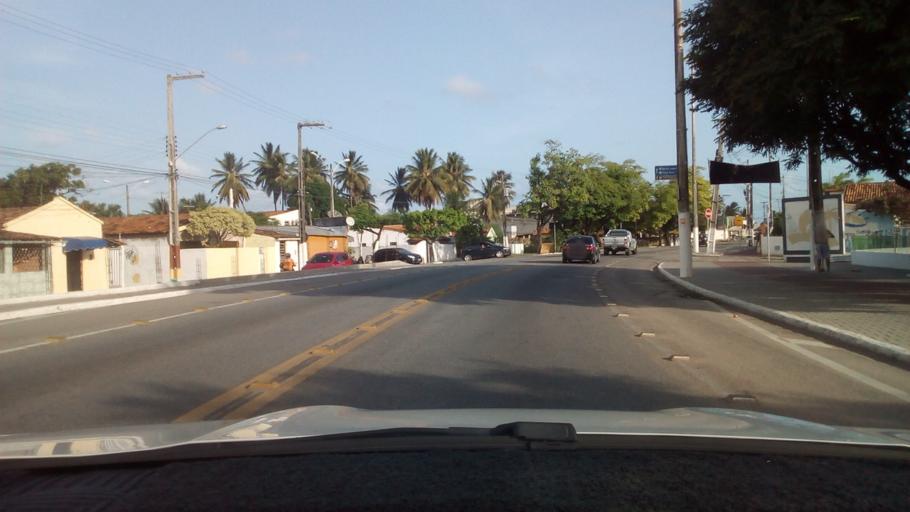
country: BR
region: Paraiba
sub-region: Cabedelo
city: Cabedelo
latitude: -6.9725
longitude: -34.8328
